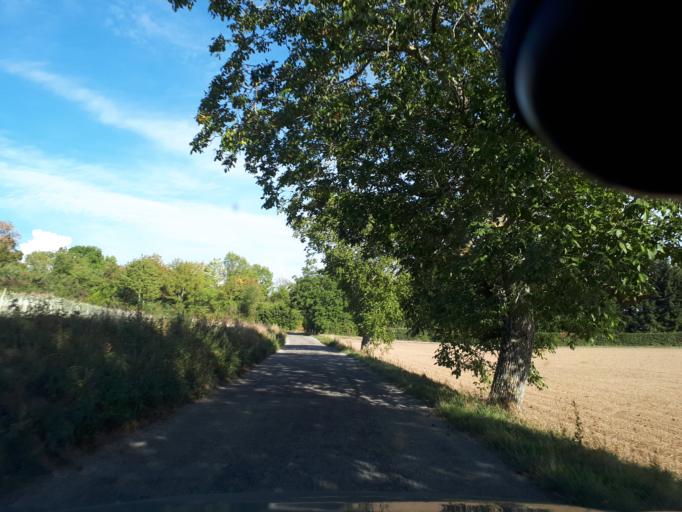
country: FR
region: Rhone-Alpes
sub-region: Departement de l'Isere
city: Chatonnay
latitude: 45.5093
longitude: 5.2234
